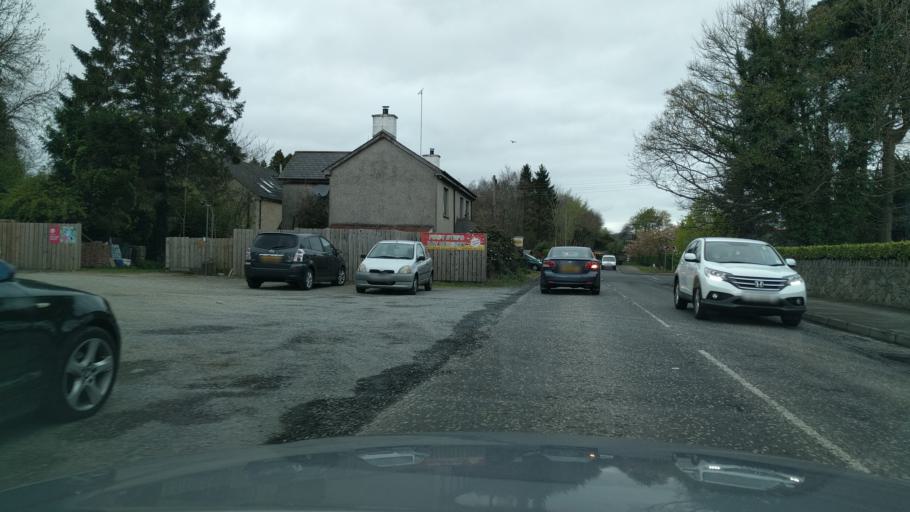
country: GB
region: Northern Ireland
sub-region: Down District
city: Warrenpoint
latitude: 54.1196
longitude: -6.2684
